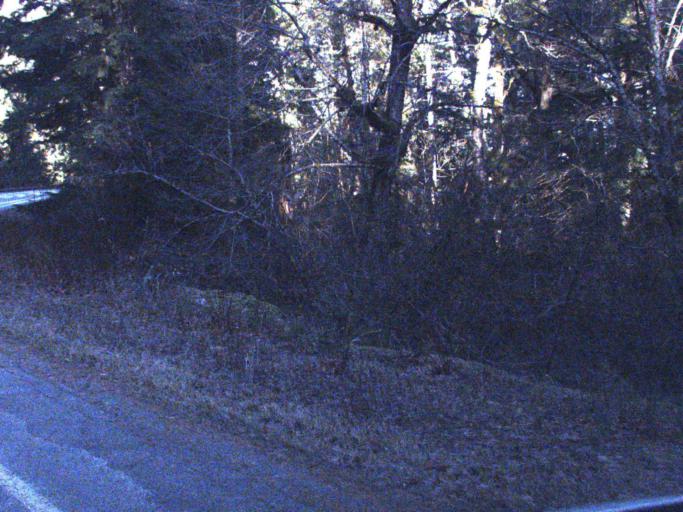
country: US
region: Washington
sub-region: Snohomish County
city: Darrington
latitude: 48.7062
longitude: -121.1139
